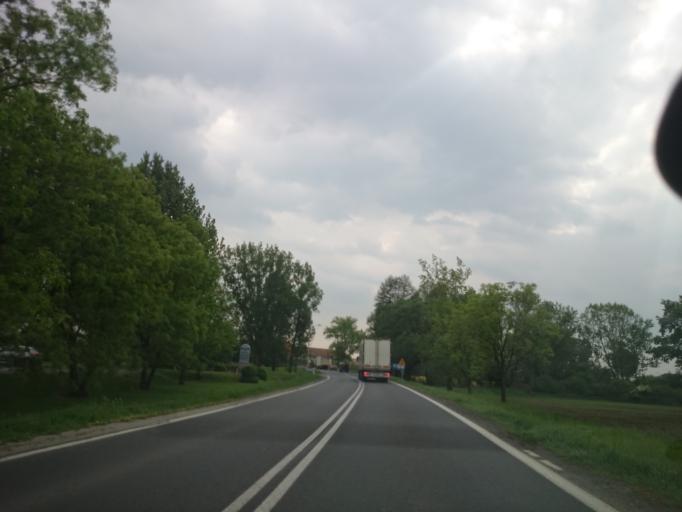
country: PL
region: Lower Silesian Voivodeship
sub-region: Powiat wroclawski
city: Kobierzyce
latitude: 50.9426
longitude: 16.9014
